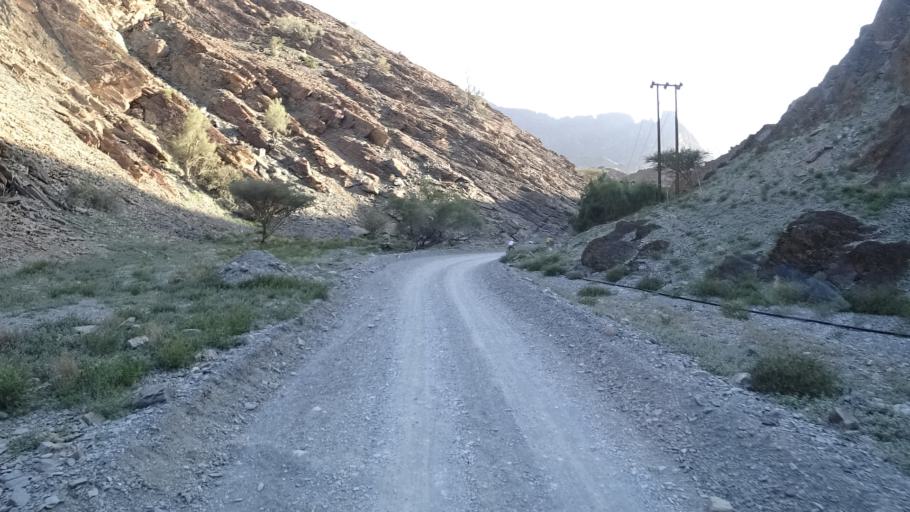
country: OM
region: Al Batinah
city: Rustaq
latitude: 23.2643
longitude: 57.3969
